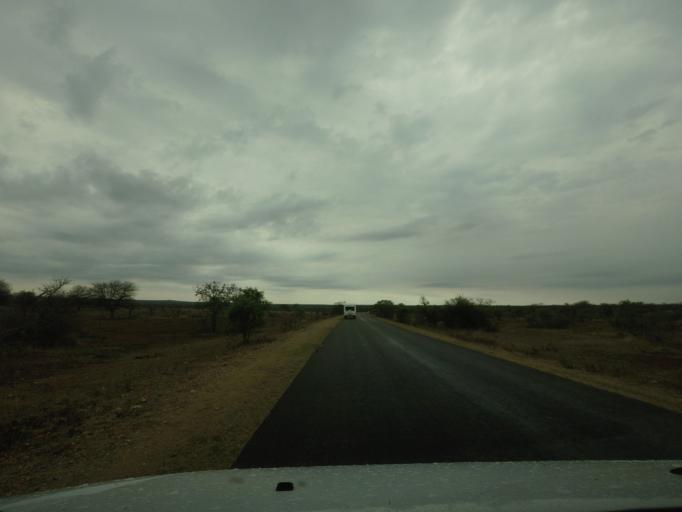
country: ZA
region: Limpopo
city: Thulamahashi
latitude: -24.4738
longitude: 31.4050
